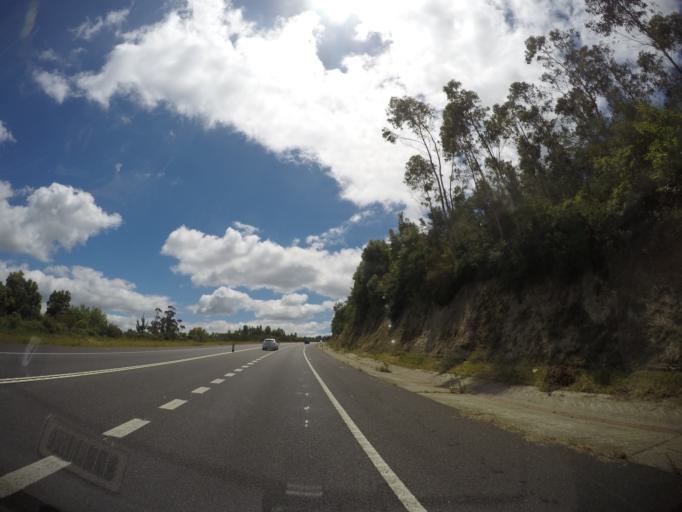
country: ES
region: Aragon
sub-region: Provincia de Zaragoza
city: El Burgo de Ebro
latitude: 41.5184
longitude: -0.7003
